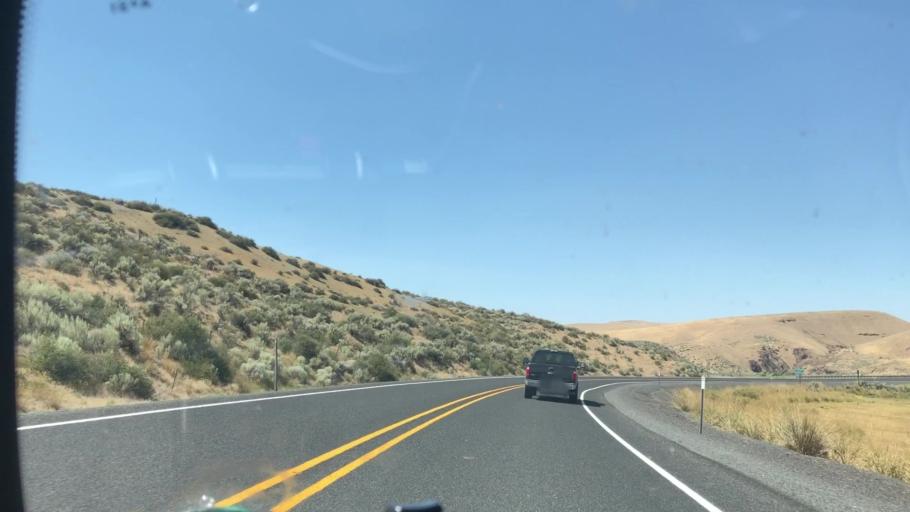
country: US
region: Idaho
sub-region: Owyhee County
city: Marsing
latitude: 43.2252
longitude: -117.0532
